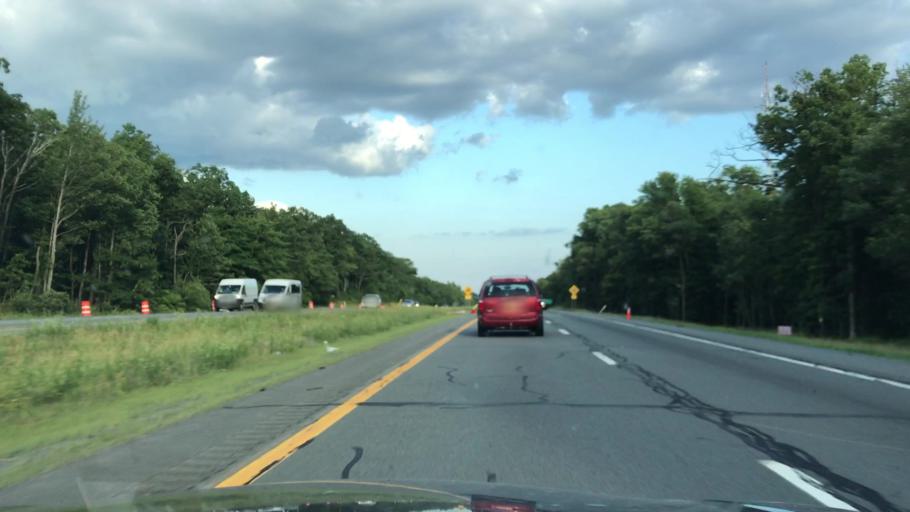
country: US
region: New York
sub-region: Sullivan County
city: Rock Hill
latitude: 41.6031
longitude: -74.5573
